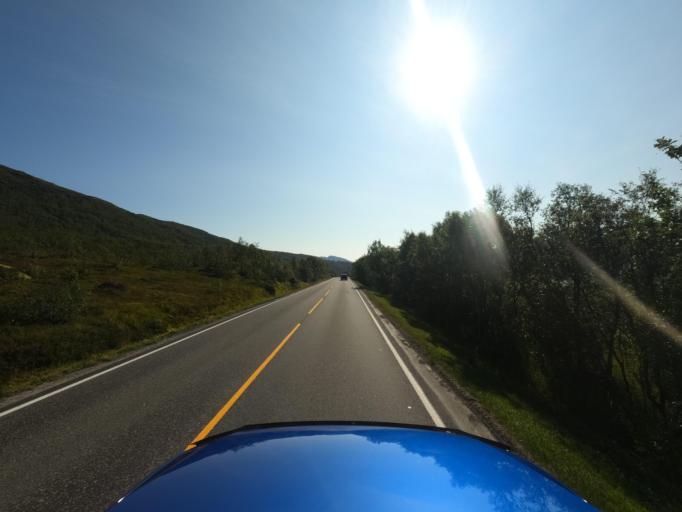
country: NO
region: Nordland
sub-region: Lodingen
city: Lodingen
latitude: 68.4990
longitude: 15.8843
